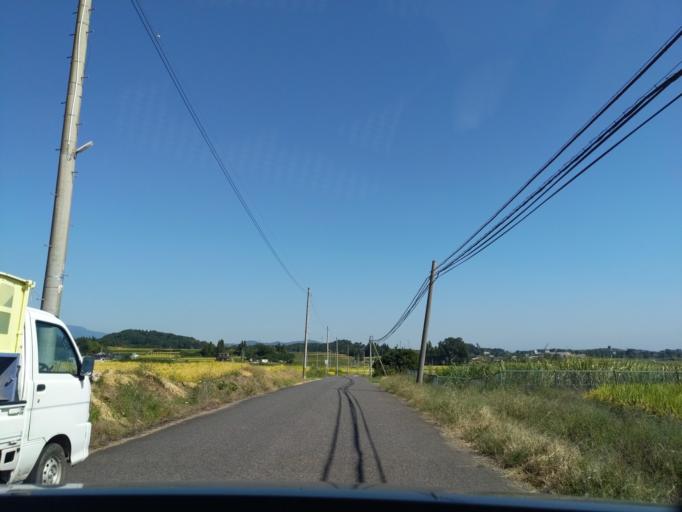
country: JP
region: Fukushima
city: Koriyama
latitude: 37.4277
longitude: 140.3080
